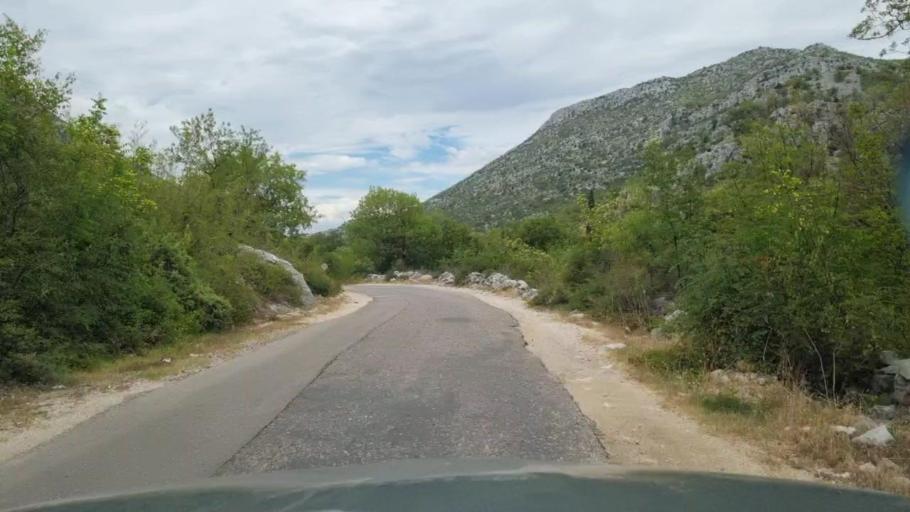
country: HR
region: Dubrovacko-Neretvanska
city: Podgora
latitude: 42.9571
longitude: 17.8006
